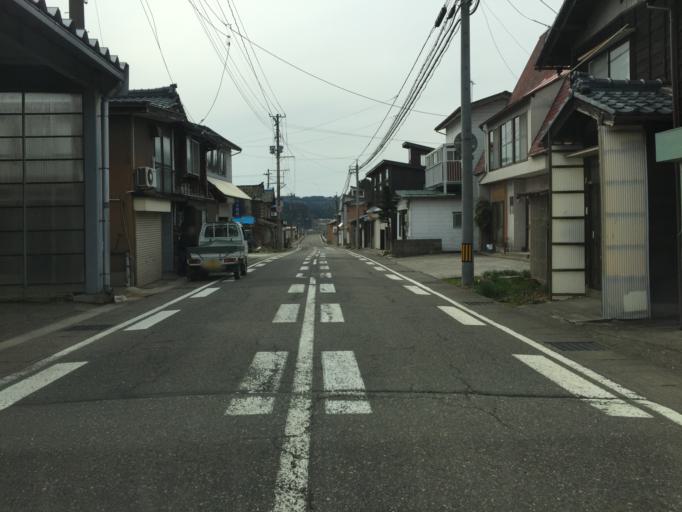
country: JP
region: Niigata
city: Tochio-honcho
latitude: 37.4446
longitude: 139.0274
